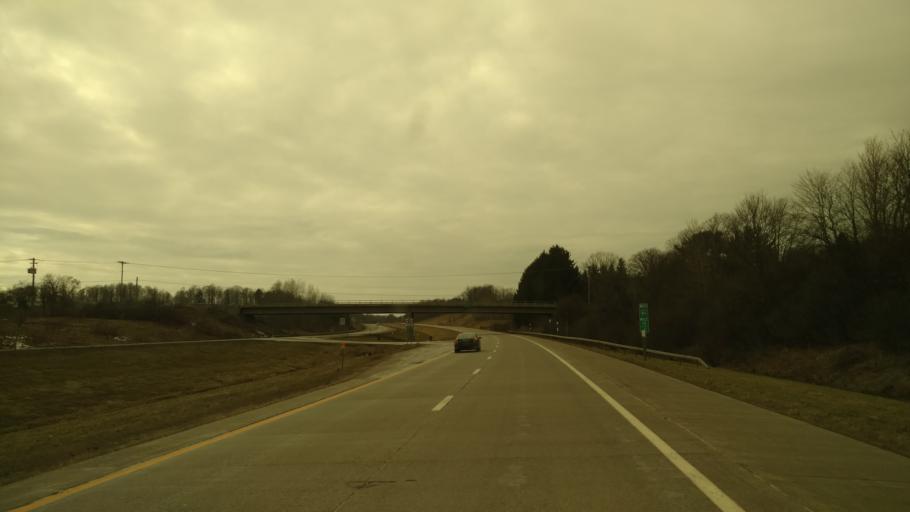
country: US
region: New York
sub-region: Chautauqua County
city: Lakewood
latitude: 42.1537
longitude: -79.4231
